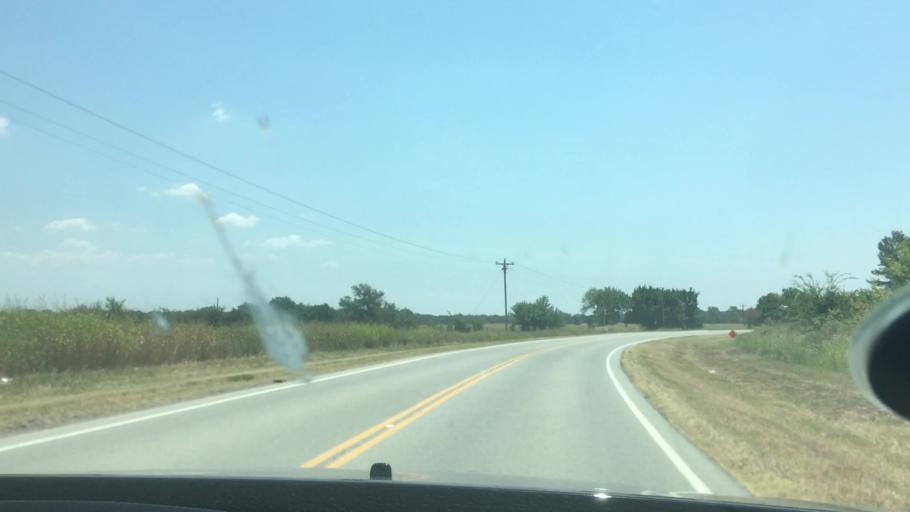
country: US
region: Oklahoma
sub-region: Coal County
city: Coalgate
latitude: 34.5797
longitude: -96.4086
